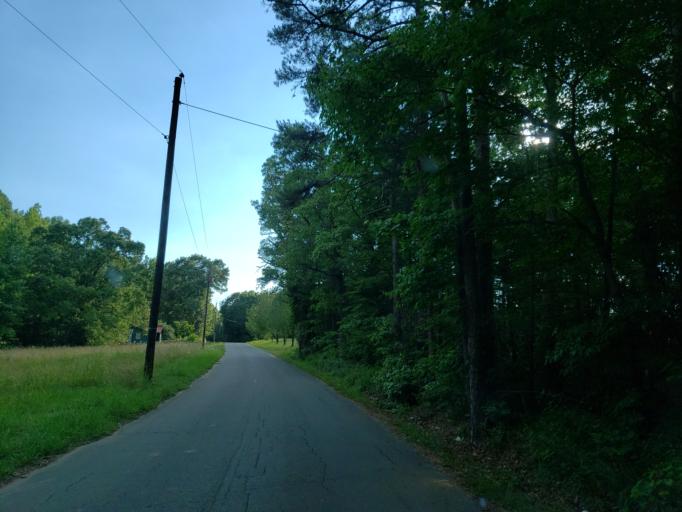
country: US
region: Georgia
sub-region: Haralson County
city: Buchanan
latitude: 33.9022
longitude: -85.2654
